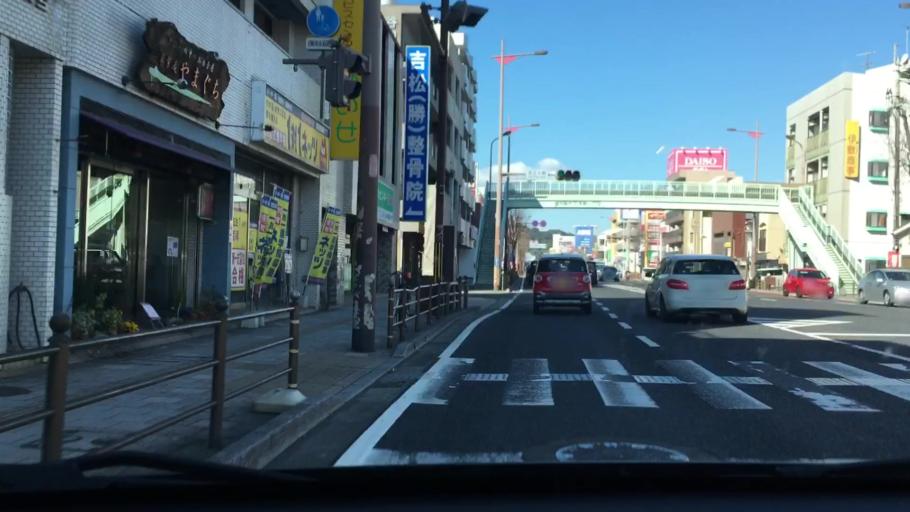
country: JP
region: Kagoshima
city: Kagoshima-shi
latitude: 31.6107
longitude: 130.5334
